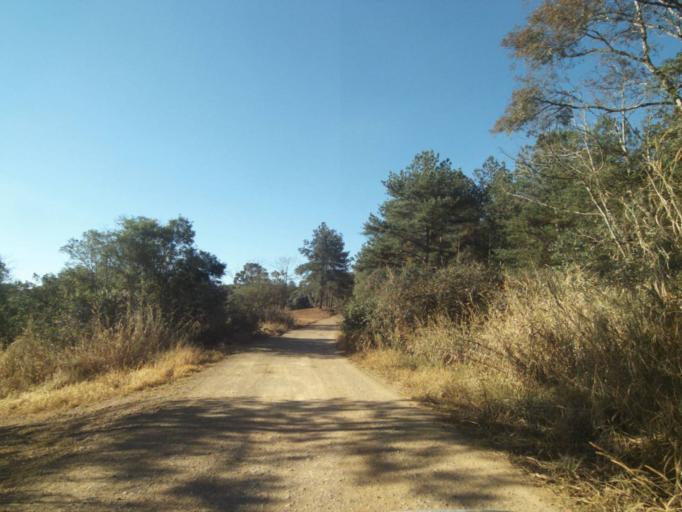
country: BR
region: Parana
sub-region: Tibagi
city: Tibagi
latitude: -24.5315
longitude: -50.4932
